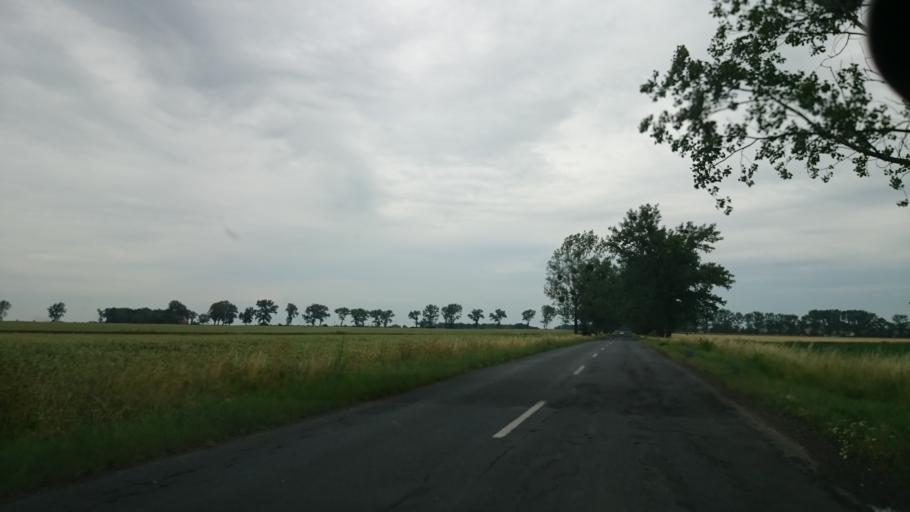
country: PL
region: Opole Voivodeship
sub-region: Powiat nyski
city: Chroscina
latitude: 50.6745
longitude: 17.3056
